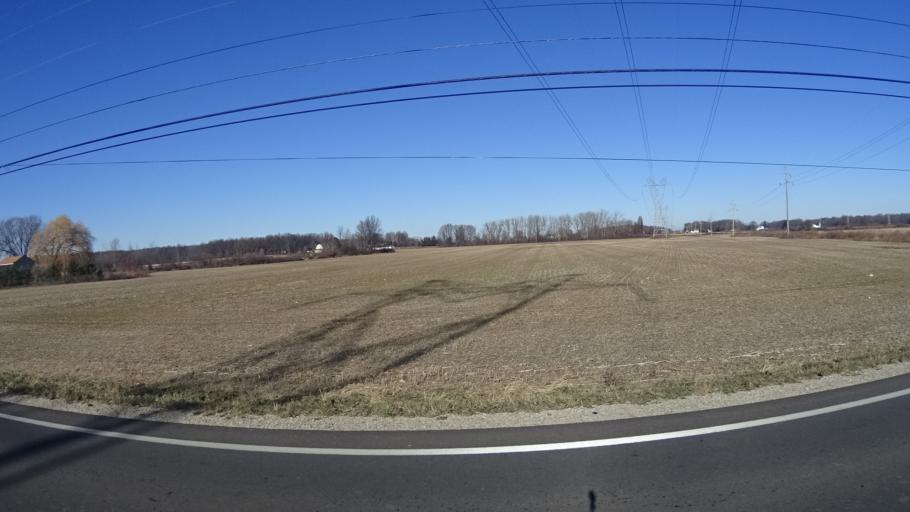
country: US
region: Ohio
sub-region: Lorain County
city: South Amherst
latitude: 41.3479
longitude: -82.2715
